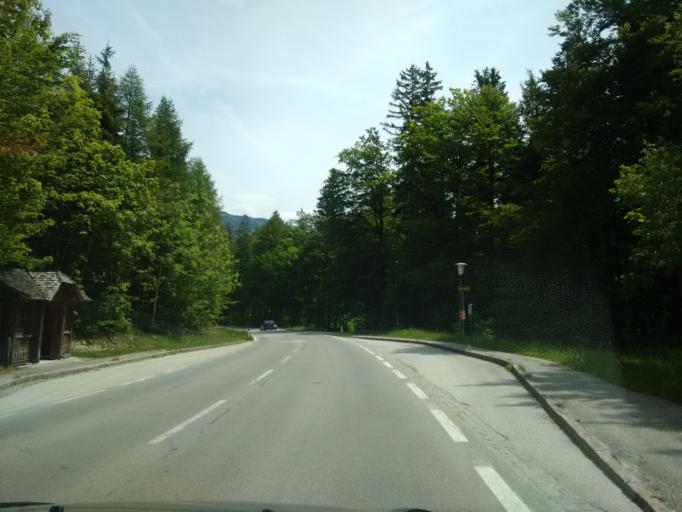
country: AT
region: Styria
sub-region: Politischer Bezirk Liezen
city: Bad Aussee
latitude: 47.6397
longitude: 13.8905
